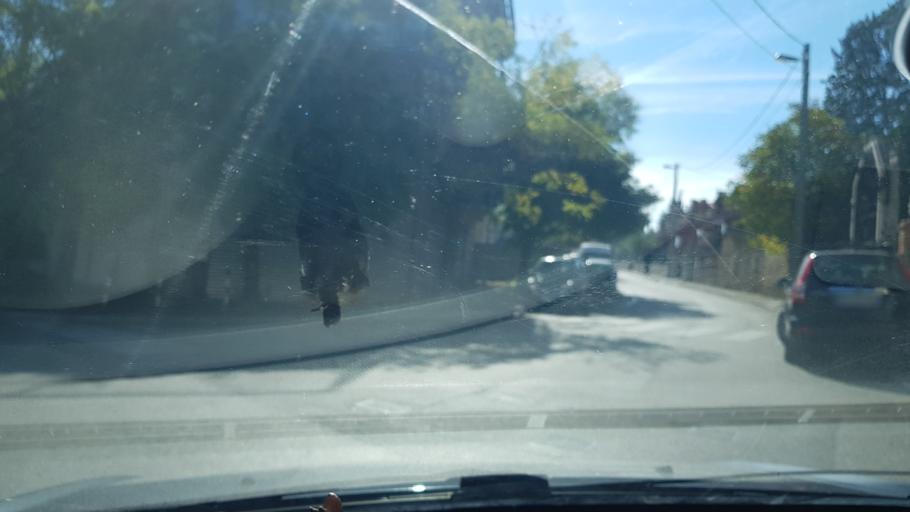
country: IT
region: Friuli Venezia Giulia
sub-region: Provincia di Trieste
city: Trieste
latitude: 45.6206
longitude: 13.7979
